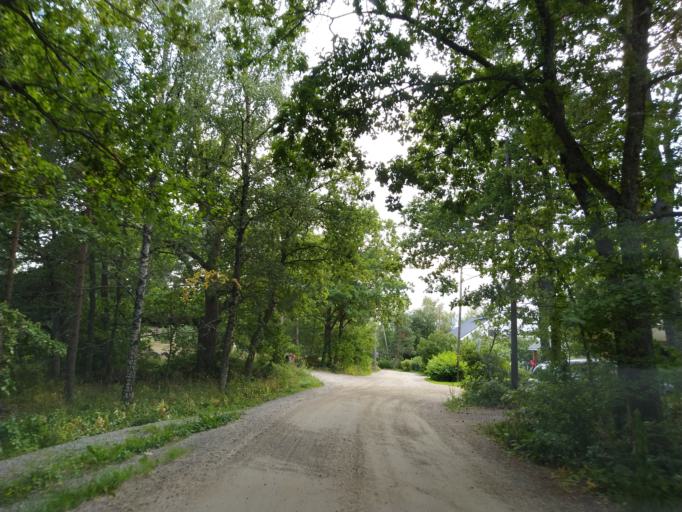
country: FI
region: Varsinais-Suomi
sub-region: Turku
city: Raisio
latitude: 60.4242
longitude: 22.1991
